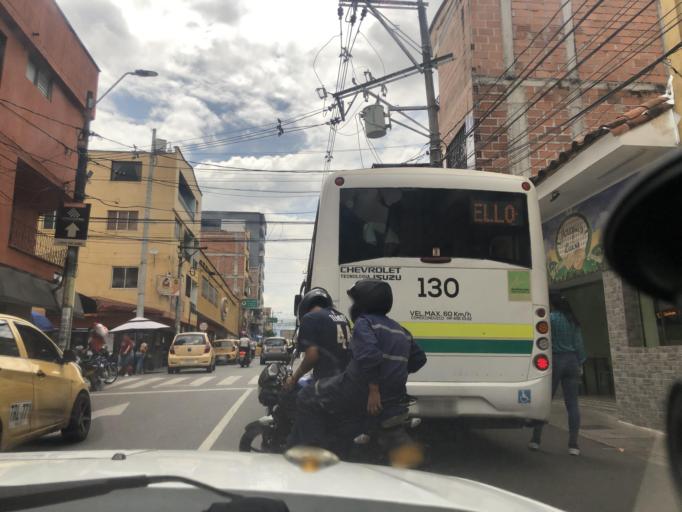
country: CO
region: Antioquia
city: Bello
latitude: 6.3394
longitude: -75.5591
